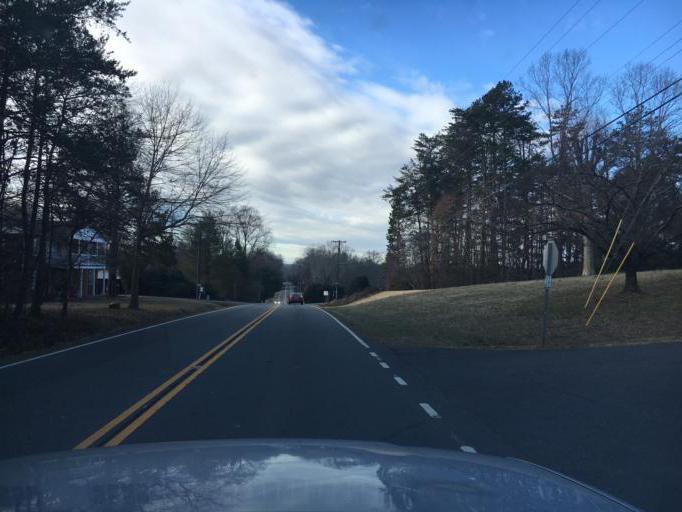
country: US
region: North Carolina
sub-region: Burke County
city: Salem
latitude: 35.7095
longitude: -81.7041
